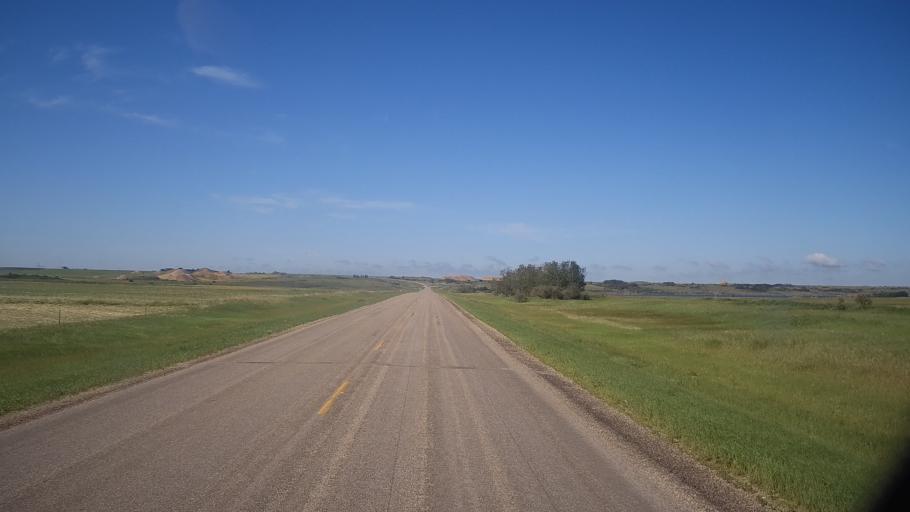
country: CA
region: Saskatchewan
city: Watrous
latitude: 51.7168
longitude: -105.3638
